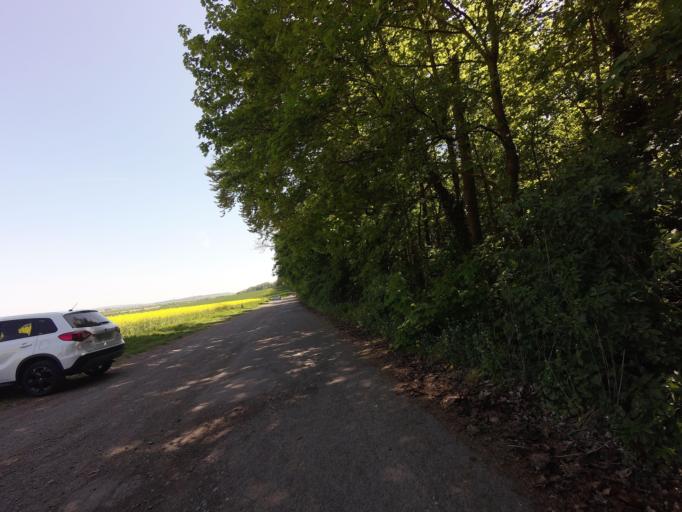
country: DE
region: Lower Saxony
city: Hildesheim
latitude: 52.1404
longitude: 9.9841
